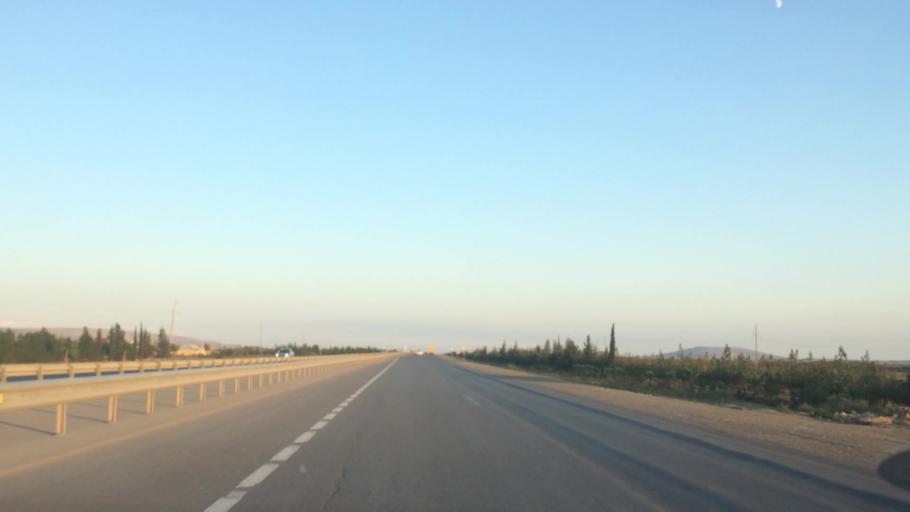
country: AZ
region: Haciqabul
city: Haciqabul
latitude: 40.0053
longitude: 49.1619
